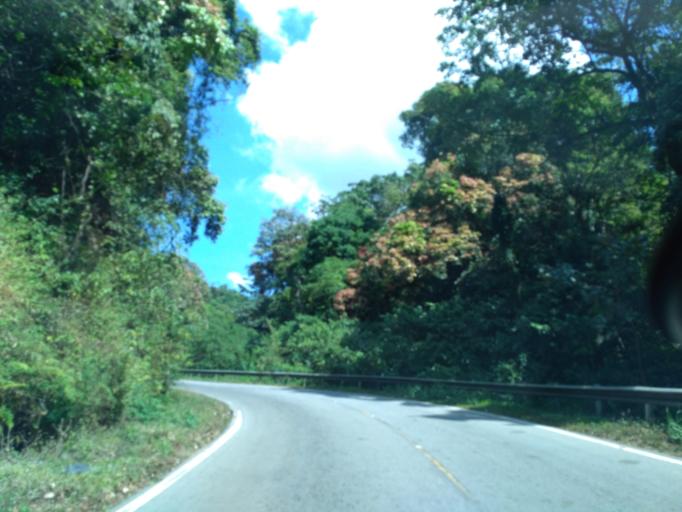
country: IN
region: Karnataka
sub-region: Kodagu
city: Madikeri
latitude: 12.4196
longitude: 75.6958
